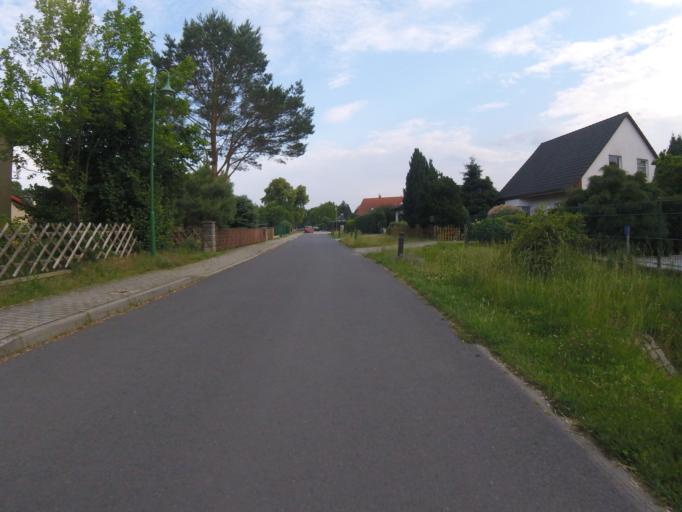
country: DE
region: Brandenburg
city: Konigs Wusterhausen
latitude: 52.2852
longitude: 13.6359
